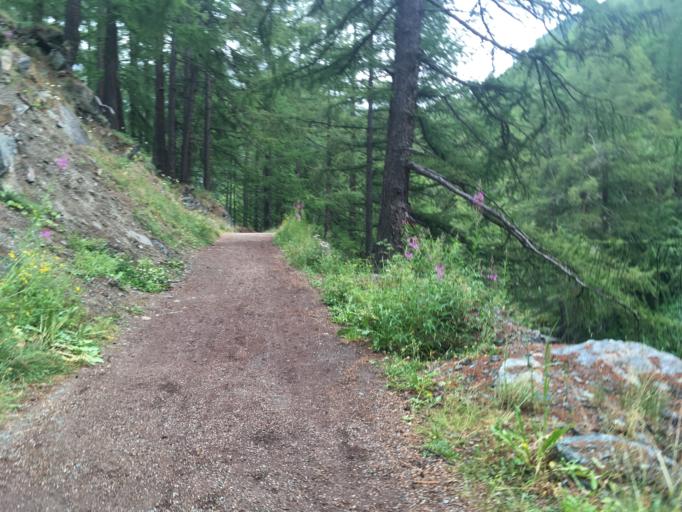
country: CH
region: Valais
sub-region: Visp District
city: Zermatt
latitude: 46.0091
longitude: 7.7325
